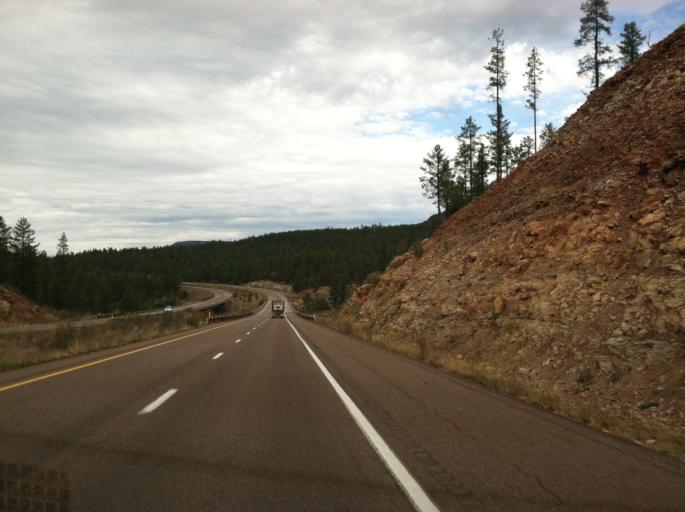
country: US
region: Arizona
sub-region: Gila County
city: Star Valley
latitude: 34.3104
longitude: -111.0243
